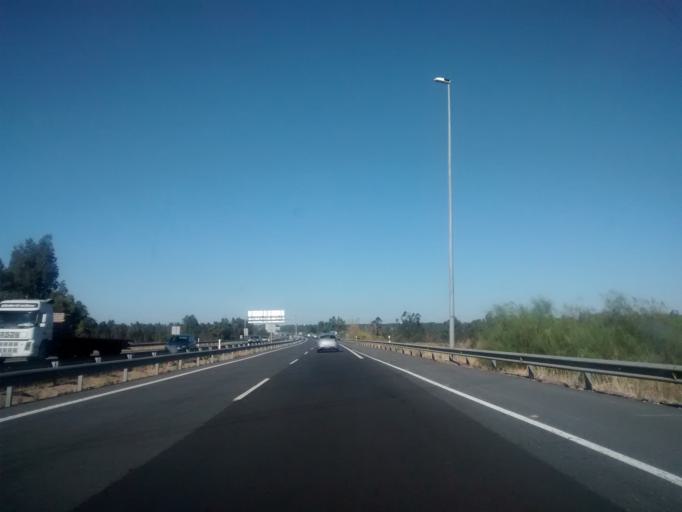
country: ES
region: Andalusia
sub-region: Provincia de Huelva
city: Gibraleon
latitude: 37.3553
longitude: -6.9688
